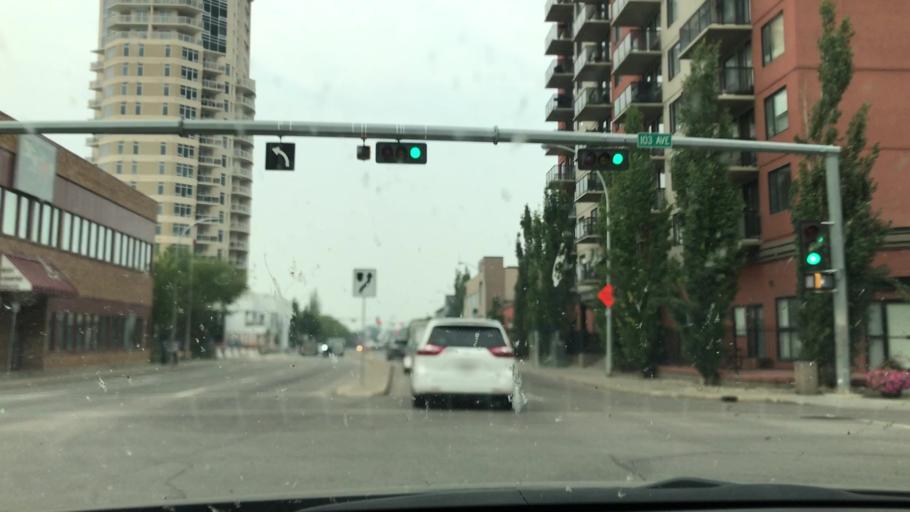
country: CA
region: Alberta
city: Edmonton
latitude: 53.5446
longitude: -113.5010
